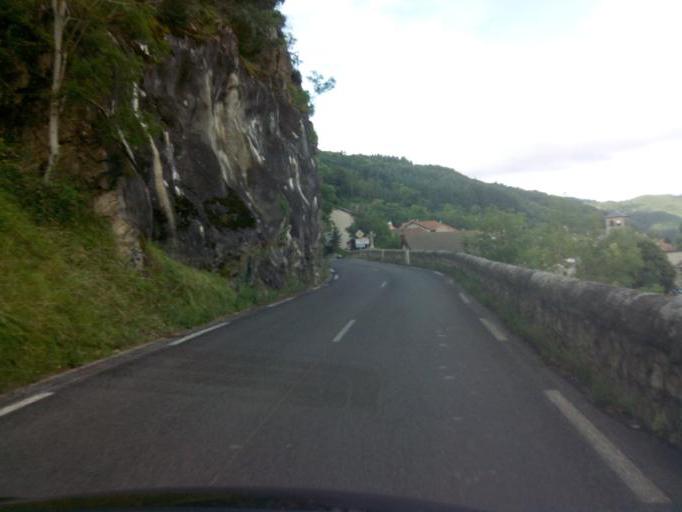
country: FR
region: Auvergne
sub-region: Departement de la Haute-Loire
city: Retournac
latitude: 45.2023
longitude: 3.9886
